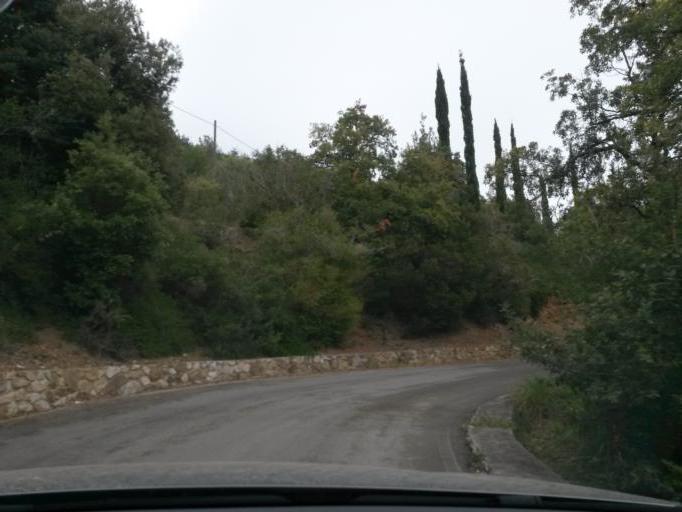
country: IT
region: Tuscany
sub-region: Provincia di Livorno
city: Capoliveri
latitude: 42.7504
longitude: 10.3651
